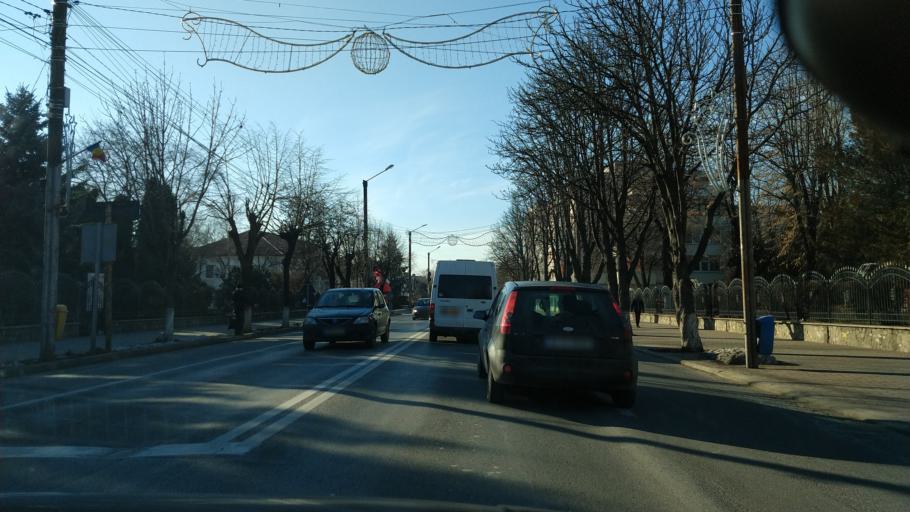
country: RO
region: Iasi
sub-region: Comuna Ion Neculce
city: Buznea
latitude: 47.2096
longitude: 27.0179
